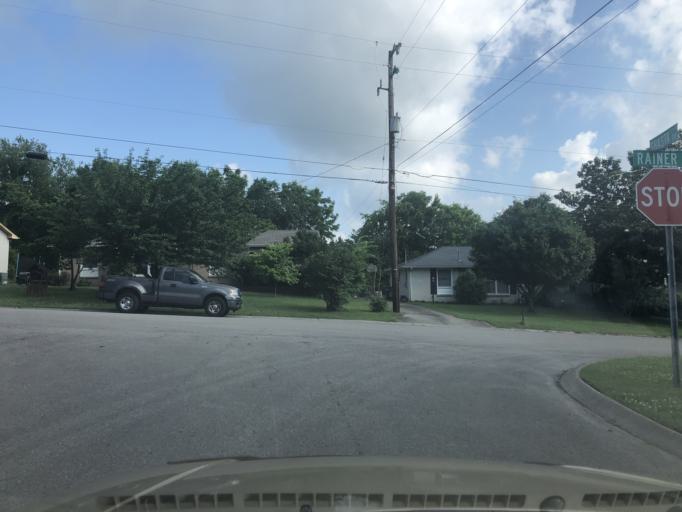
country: US
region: Tennessee
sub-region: Wilson County
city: Green Hill
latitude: 36.2278
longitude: -86.5895
